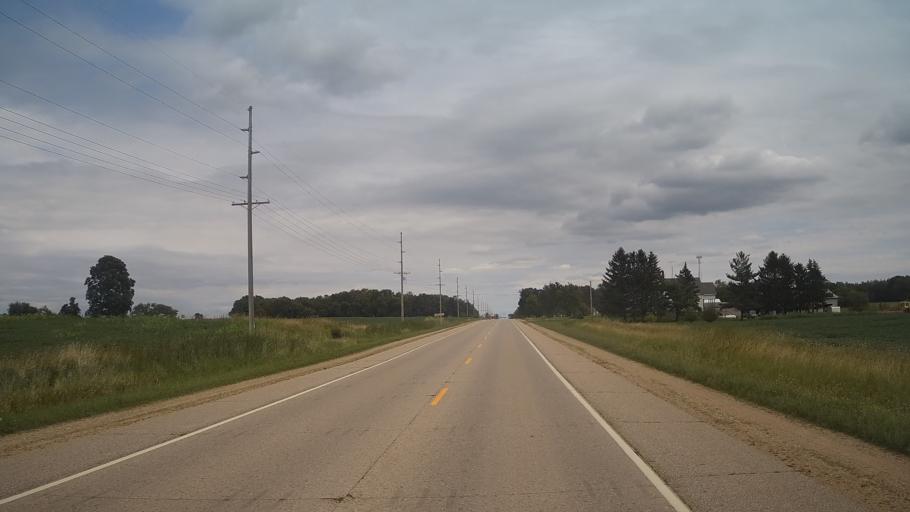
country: US
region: Wisconsin
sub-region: Waushara County
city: Redgranite
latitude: 44.0410
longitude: -89.0055
